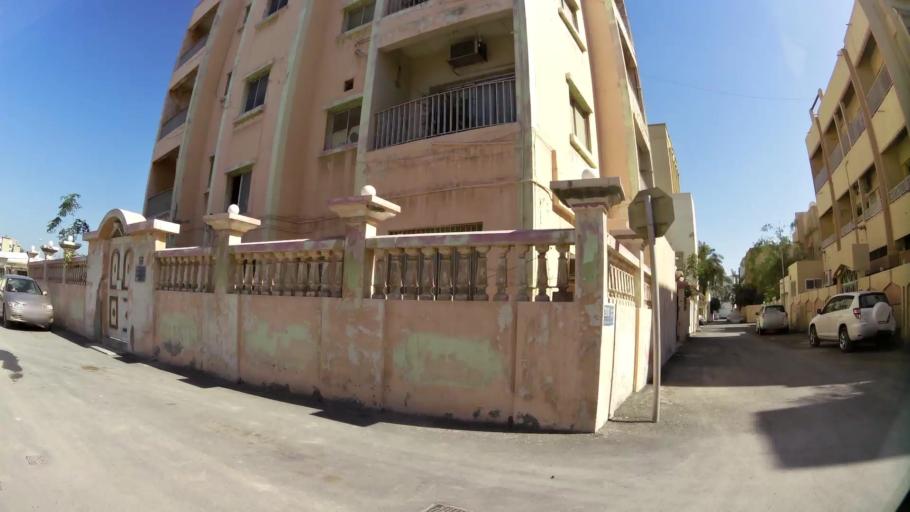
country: BH
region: Manama
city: Manama
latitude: 26.2141
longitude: 50.5678
